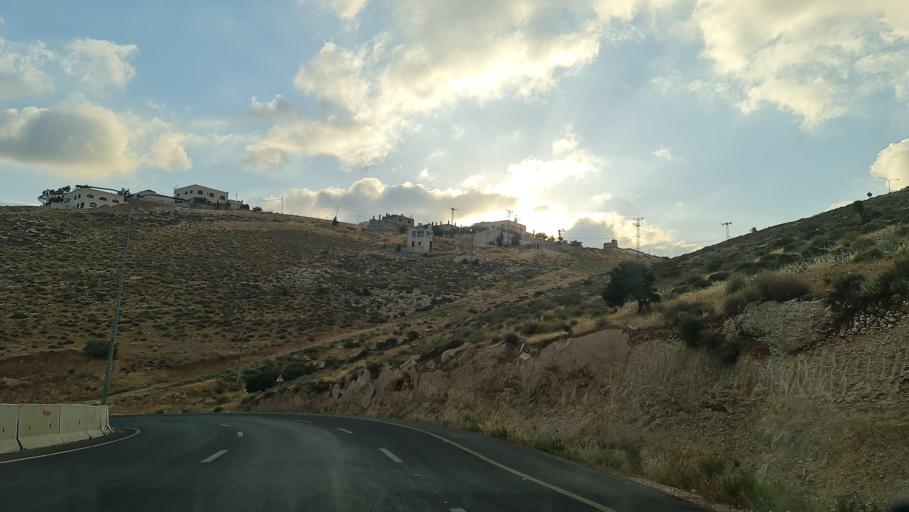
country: JO
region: Zarqa
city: Russeifa
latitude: 32.0928
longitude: 35.9616
